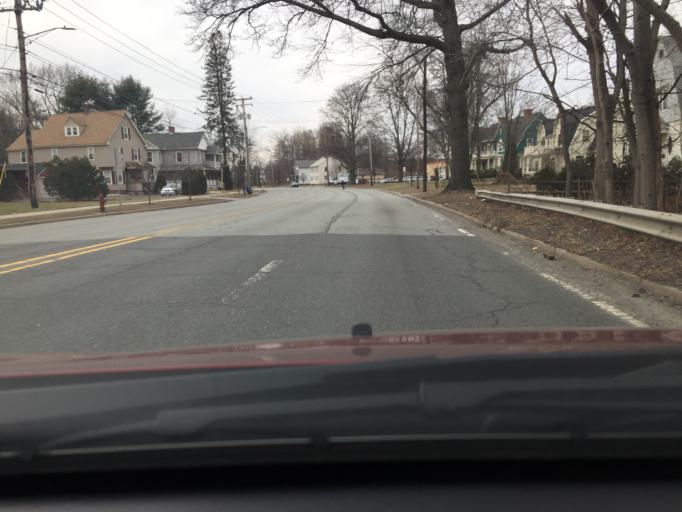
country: US
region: Massachusetts
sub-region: Hampden County
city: Westfield
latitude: 42.1168
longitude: -72.7336
